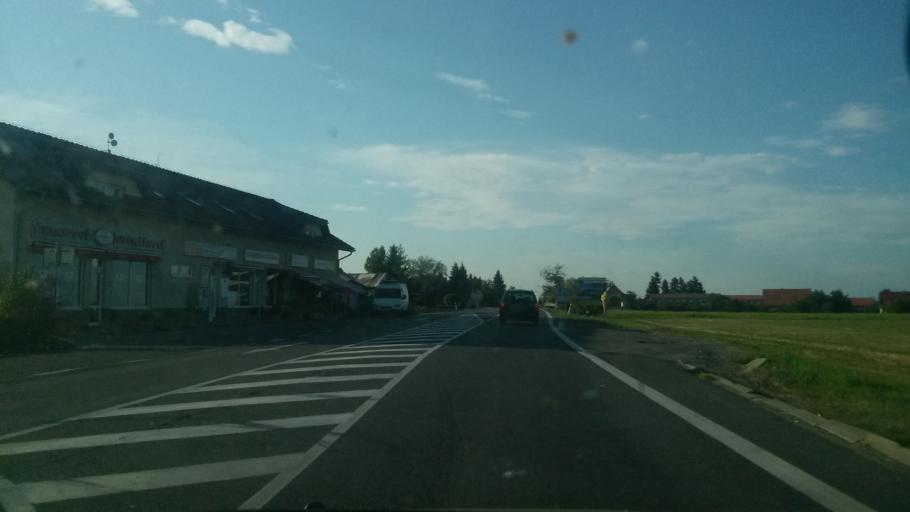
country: CZ
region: Central Bohemia
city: Vestec
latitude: 49.9732
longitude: 14.5028
